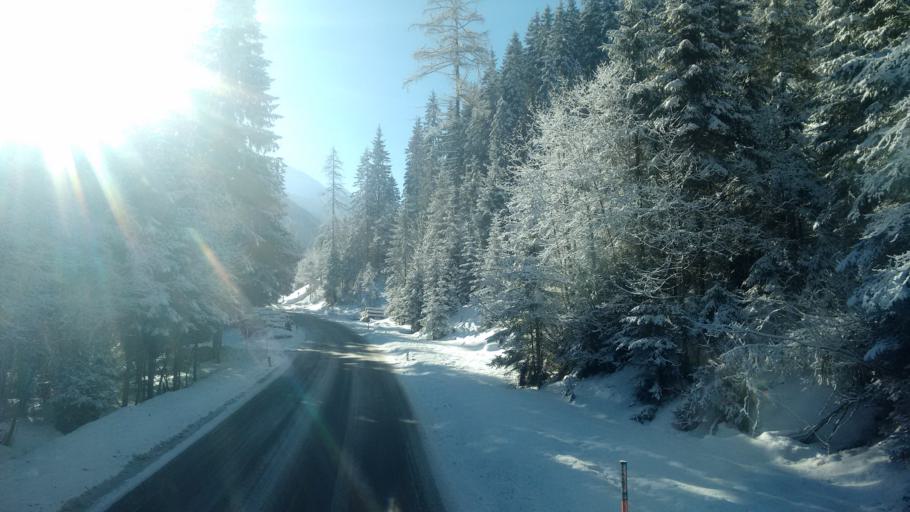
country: AT
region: Salzburg
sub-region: Politischer Bezirk Sankt Johann im Pongau
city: Altenmarkt im Pongau
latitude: 47.3464
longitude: 13.4311
